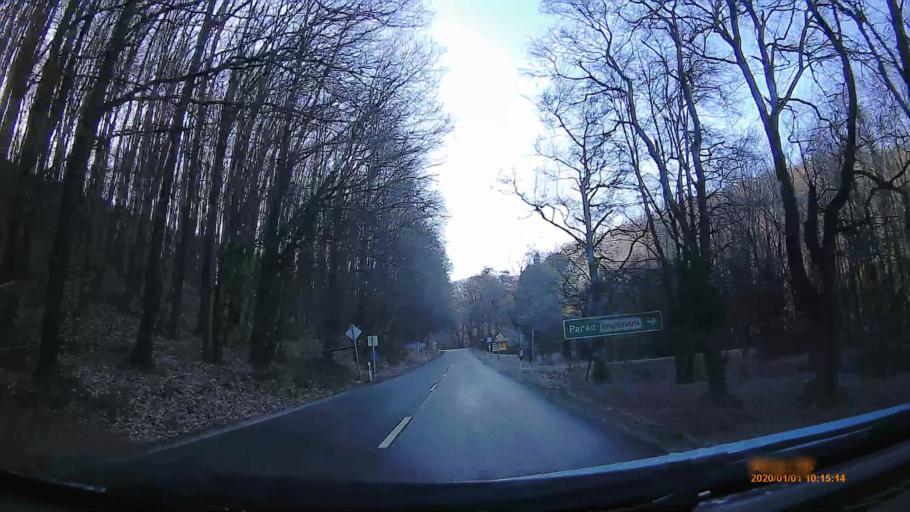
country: HU
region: Heves
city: Paradsasvar
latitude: 47.9181
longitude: 19.9948
